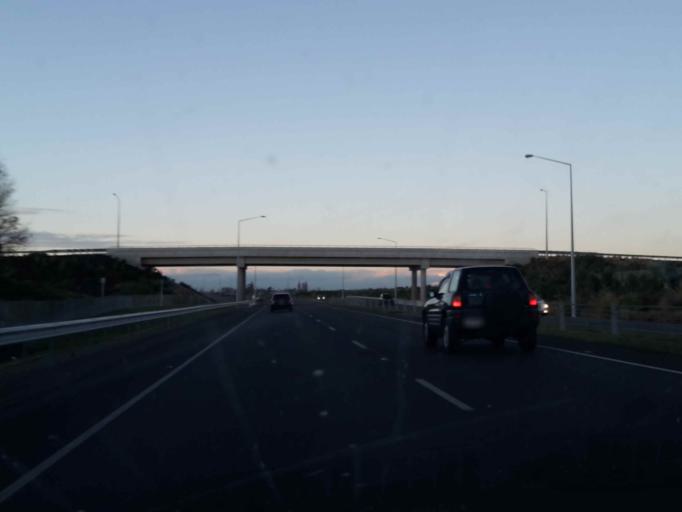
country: NZ
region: Canterbury
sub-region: Selwyn District
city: Prebbleton
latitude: -43.5600
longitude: 172.5633
